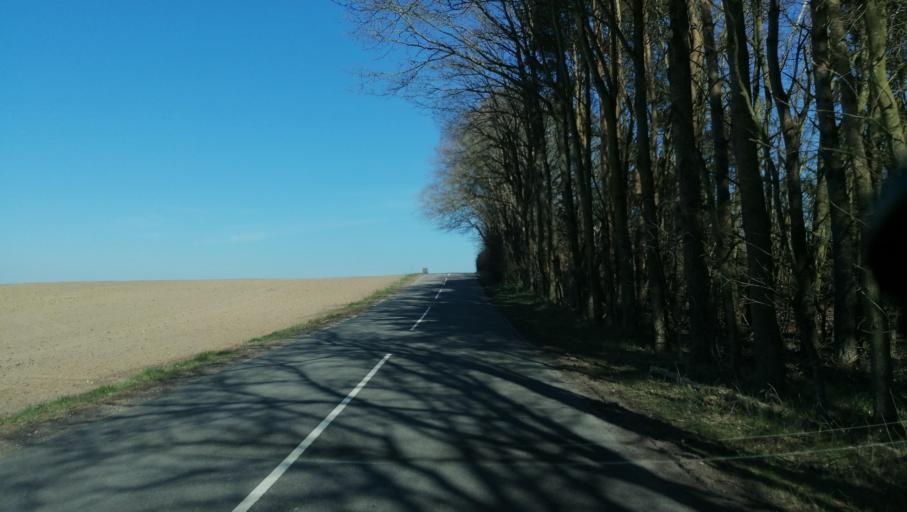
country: DK
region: Zealand
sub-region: Odsherred Kommune
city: Asnaes
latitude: 55.8333
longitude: 11.5412
